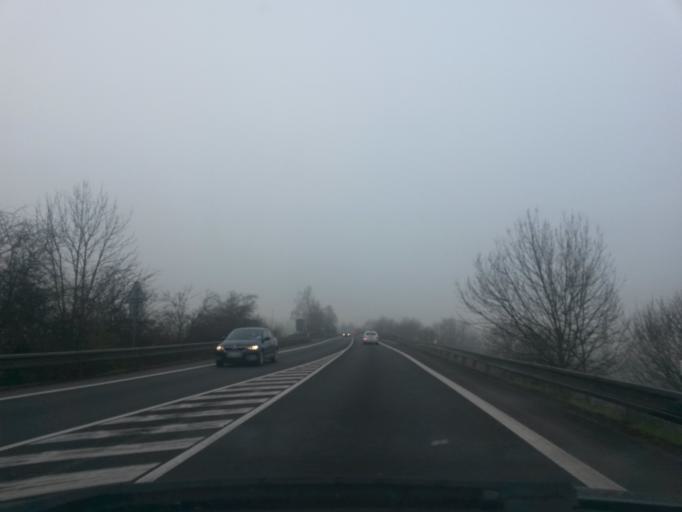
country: CZ
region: Ustecky
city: Cerncice
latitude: 50.3355
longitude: 13.8367
